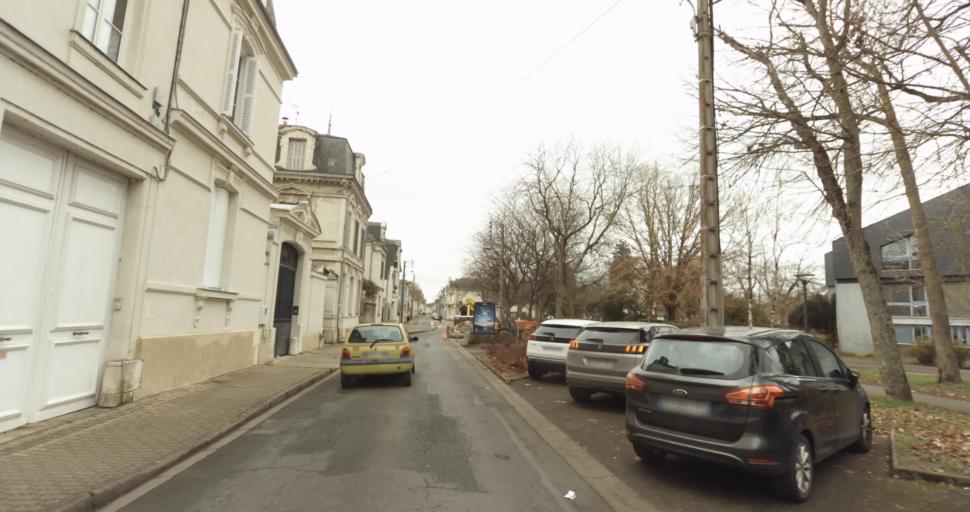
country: FR
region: Pays de la Loire
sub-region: Departement de Maine-et-Loire
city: Saumur
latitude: 47.2560
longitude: -0.0806
